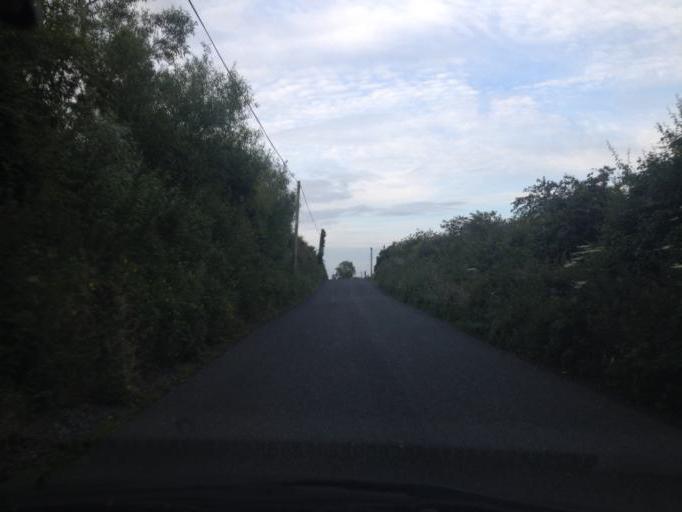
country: IE
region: Connaught
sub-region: Sligo
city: Strandhill
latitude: 54.3872
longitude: -8.5500
